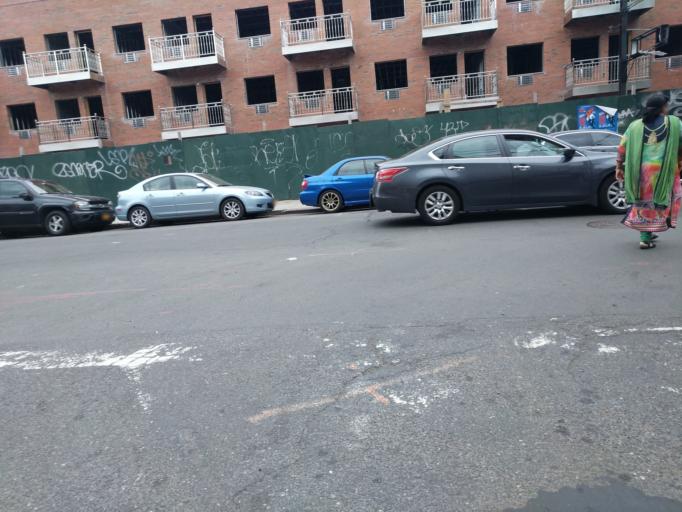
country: US
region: New York
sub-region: Queens County
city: Long Island City
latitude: 40.7430
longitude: -73.8759
